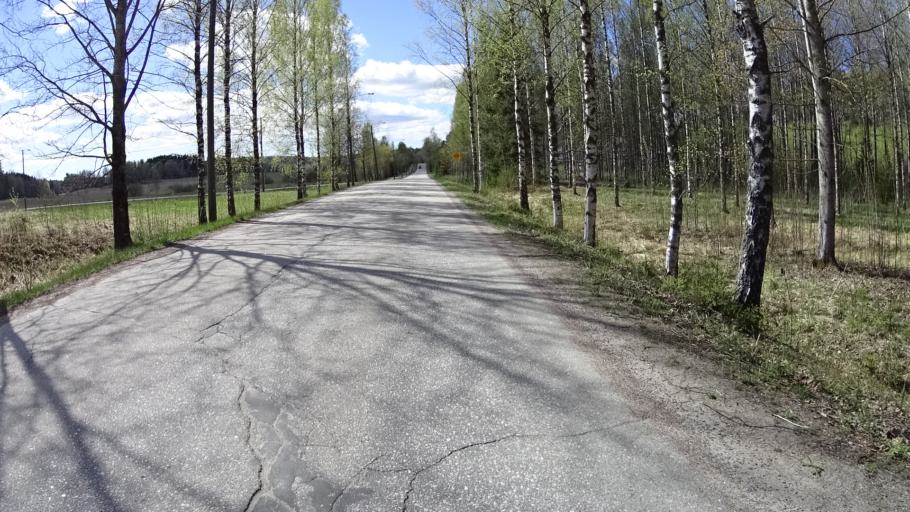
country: FI
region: Uusimaa
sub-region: Helsinki
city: Vihti
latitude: 60.3800
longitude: 24.5127
